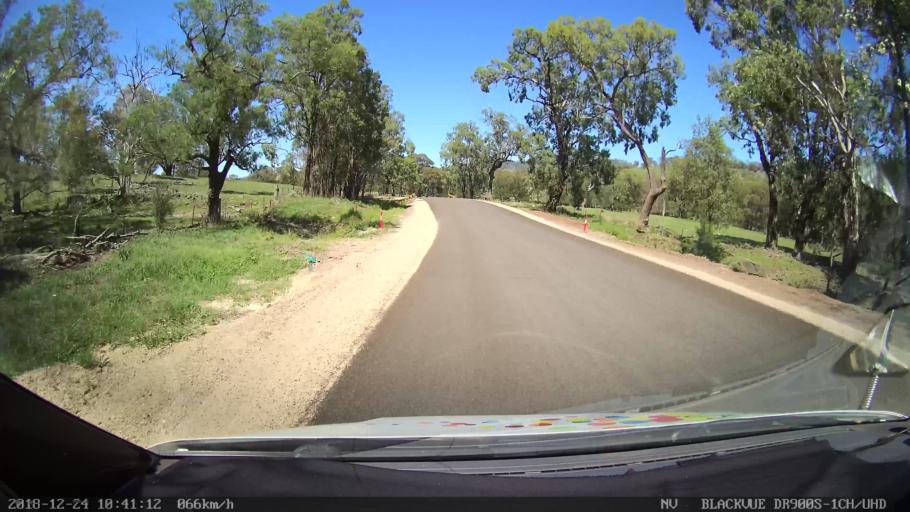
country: AU
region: New South Wales
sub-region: Upper Hunter Shire
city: Merriwa
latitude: -31.8672
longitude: 150.4610
